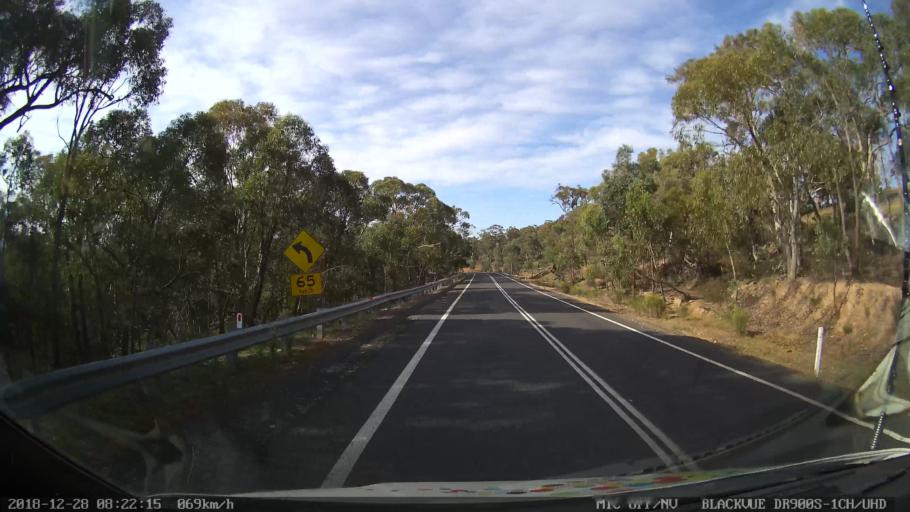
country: AU
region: New South Wales
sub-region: Blayney
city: Blayney
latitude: -33.8914
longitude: 149.3488
